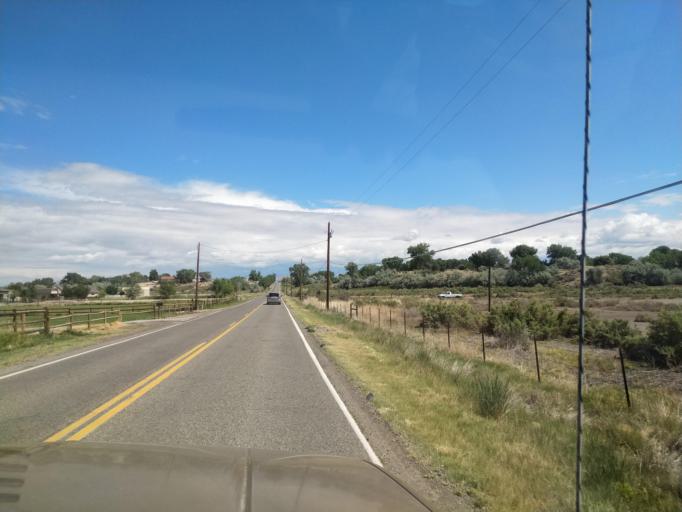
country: US
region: Colorado
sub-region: Mesa County
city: Redlands
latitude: 39.1247
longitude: -108.6081
